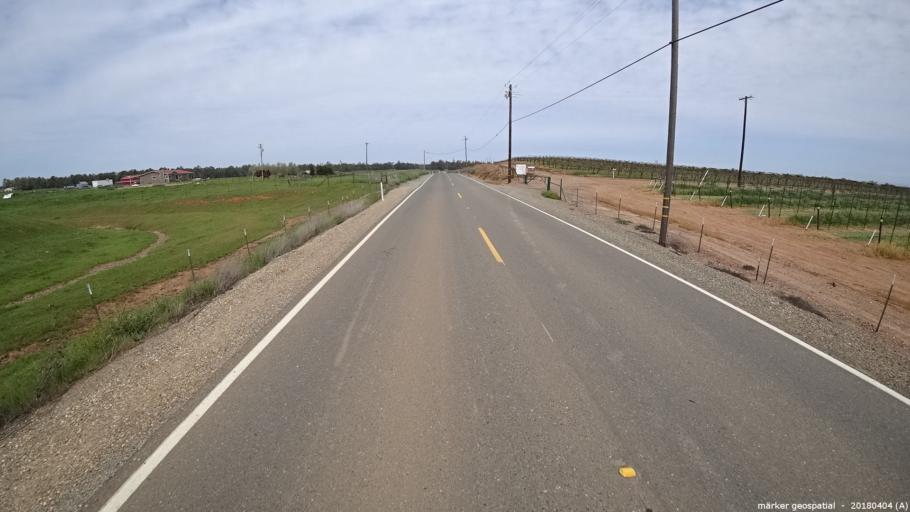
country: US
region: California
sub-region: Sacramento County
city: Clay
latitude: 38.2850
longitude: -121.1714
